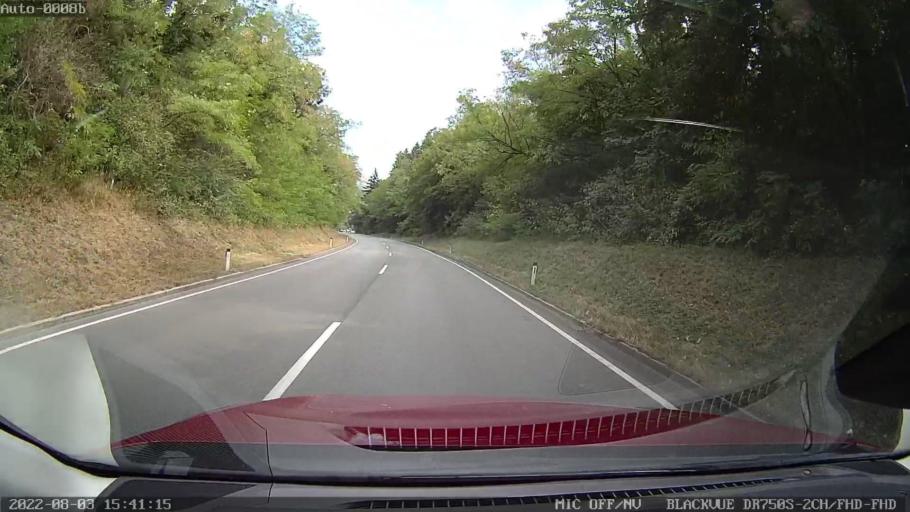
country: SI
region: Nova Gorica
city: Kromberk
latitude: 45.9557
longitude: 13.6833
